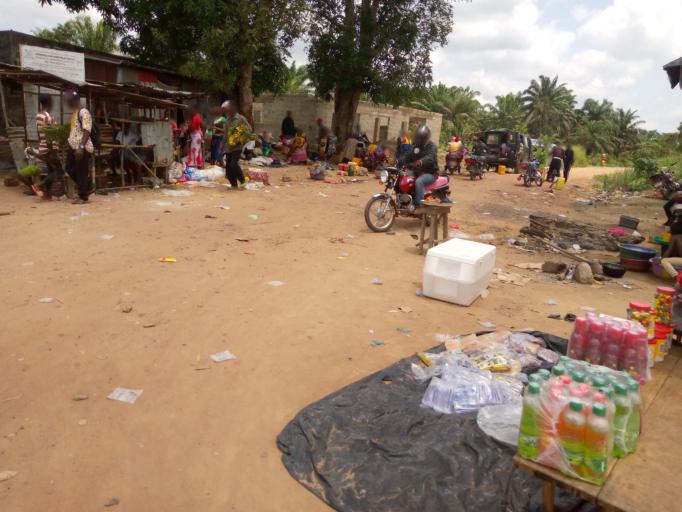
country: SL
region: Western Area
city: Waterloo
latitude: 8.3701
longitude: -12.9601
